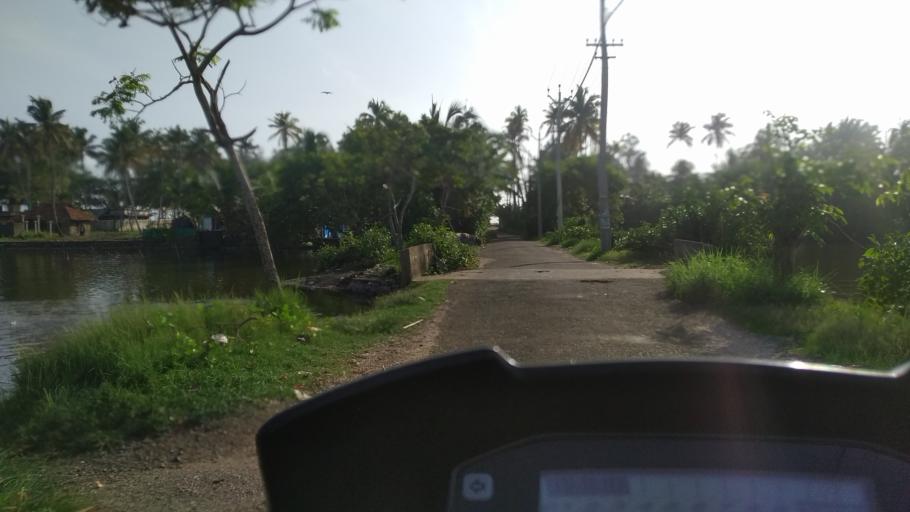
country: IN
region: Kerala
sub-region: Thrissur District
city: Kodungallur
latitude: 10.1278
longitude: 76.1844
